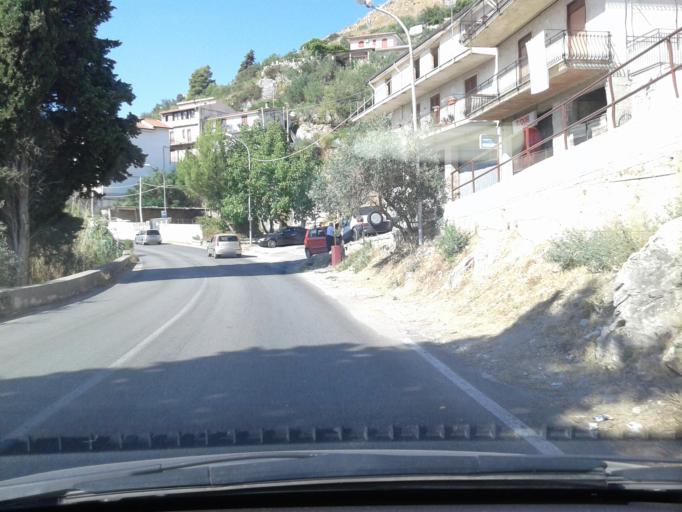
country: IT
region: Sicily
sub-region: Palermo
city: Pioppo
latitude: 38.0436
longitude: 13.2204
